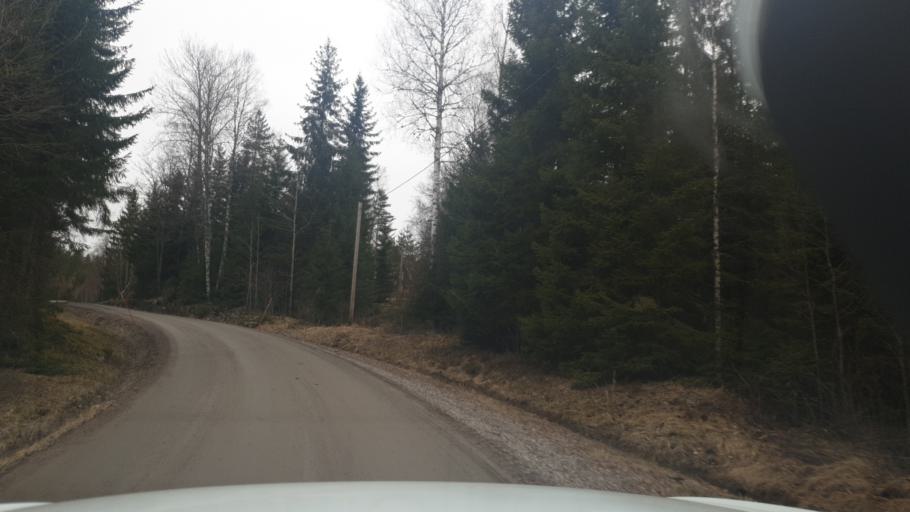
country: NO
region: Ostfold
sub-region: Romskog
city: Romskog
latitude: 59.7043
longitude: 12.0530
